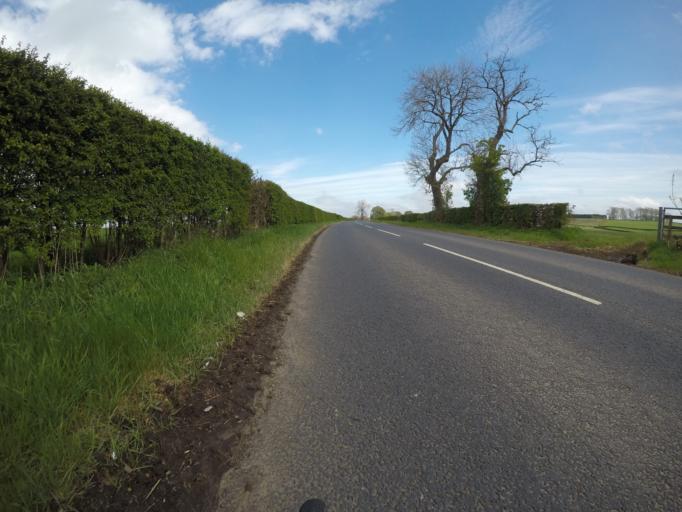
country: GB
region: Scotland
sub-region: East Ayrshire
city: Crosshouse
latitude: 55.6494
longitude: -4.5703
